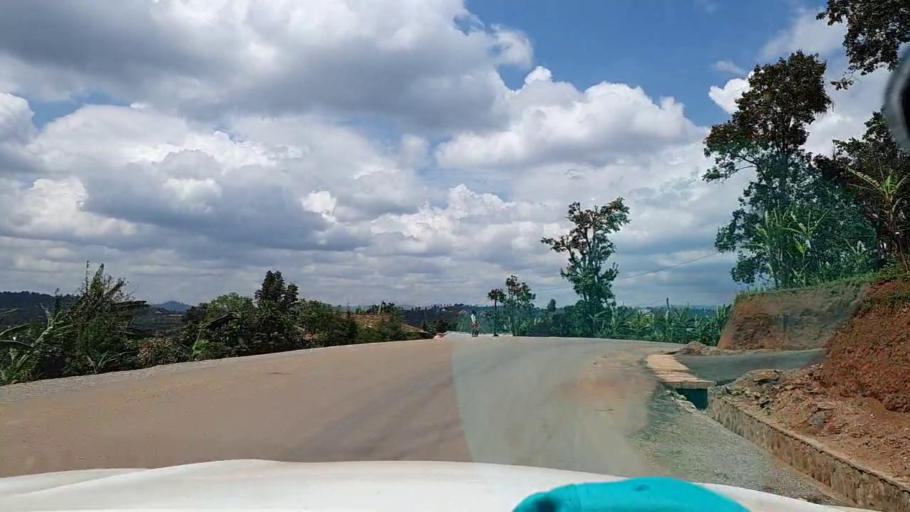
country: RW
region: Southern Province
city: Nzega
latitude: -2.6470
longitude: 29.5684
